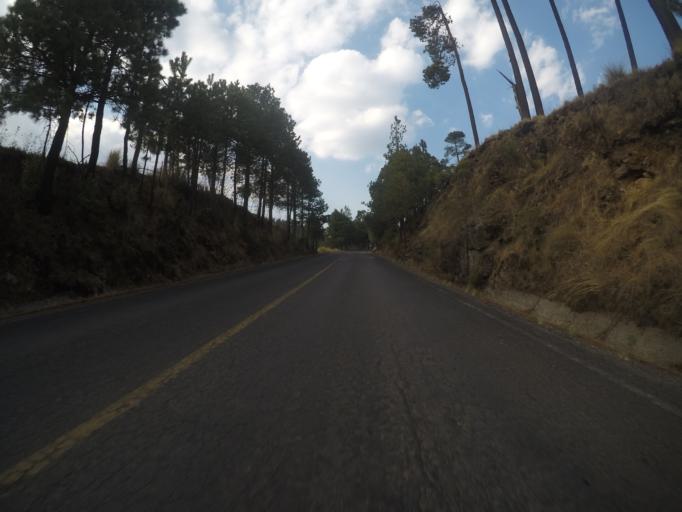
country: MX
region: Mexico
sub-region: Xalatlaco
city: San Juan Tomasquillo Herradura
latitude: 19.1858
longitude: -99.3523
